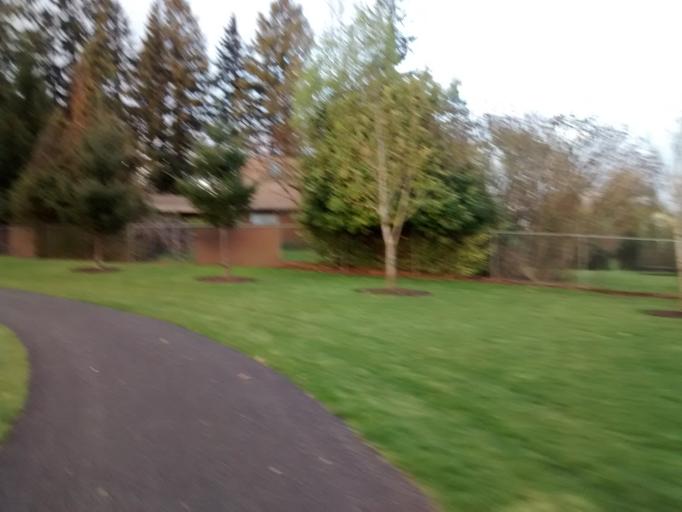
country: US
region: Washington
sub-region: Clark County
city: Barberton
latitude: 45.6939
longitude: -122.6233
